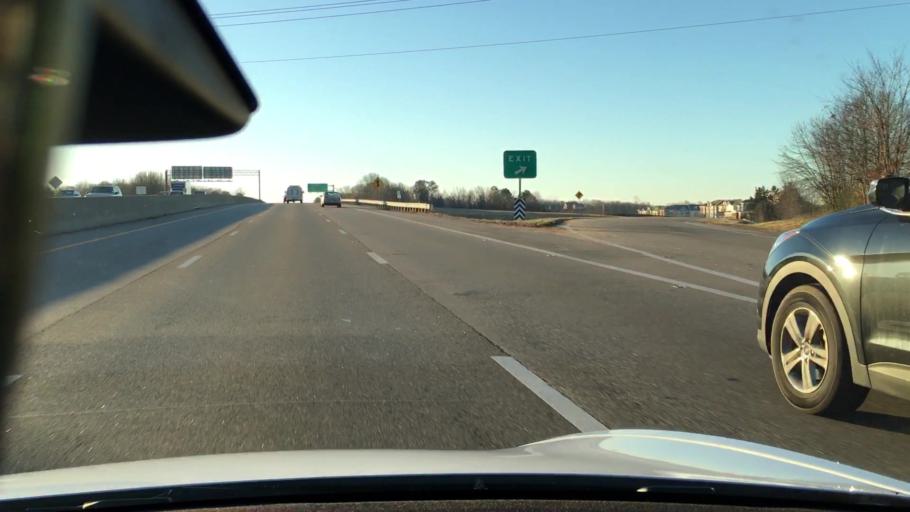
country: US
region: Virginia
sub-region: Chesterfield County
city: Bon Air
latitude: 37.5039
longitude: -77.5260
